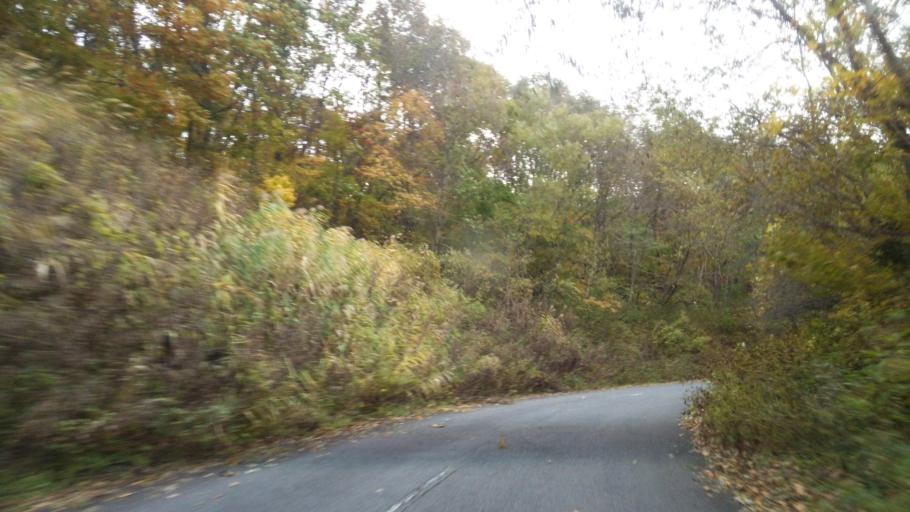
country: JP
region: Fukushima
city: Kitakata
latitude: 37.3988
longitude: 139.7505
